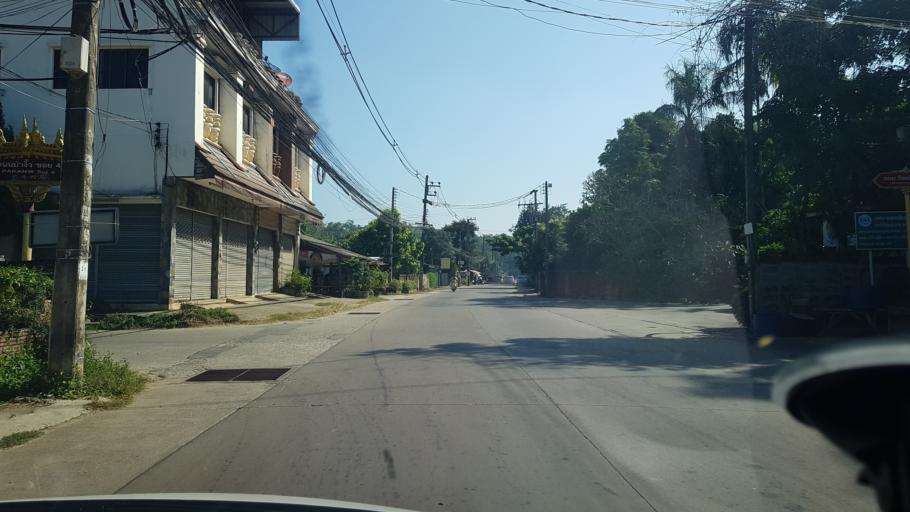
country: TH
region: Chiang Rai
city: Chiang Rai
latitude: 19.9079
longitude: 99.7957
